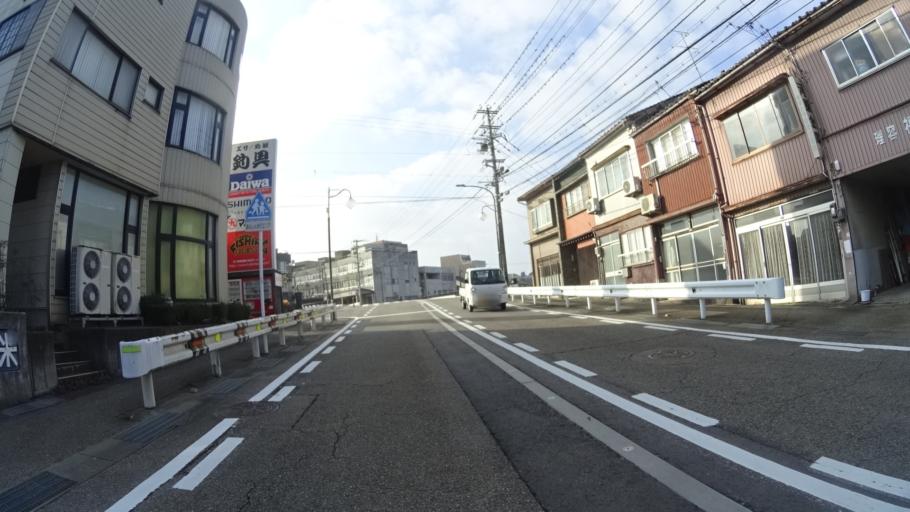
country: JP
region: Toyama
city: Himi
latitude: 36.8617
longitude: 136.9858
